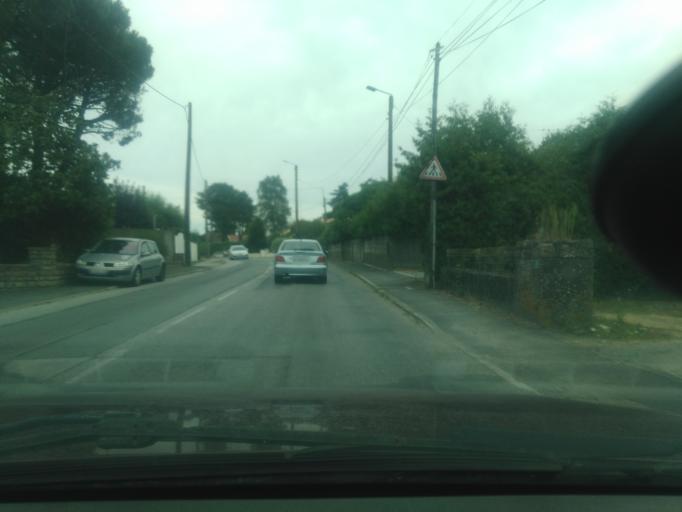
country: FR
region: Poitou-Charentes
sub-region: Departement des Deux-Sevres
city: Parthenay
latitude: 46.6362
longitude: -0.2453
